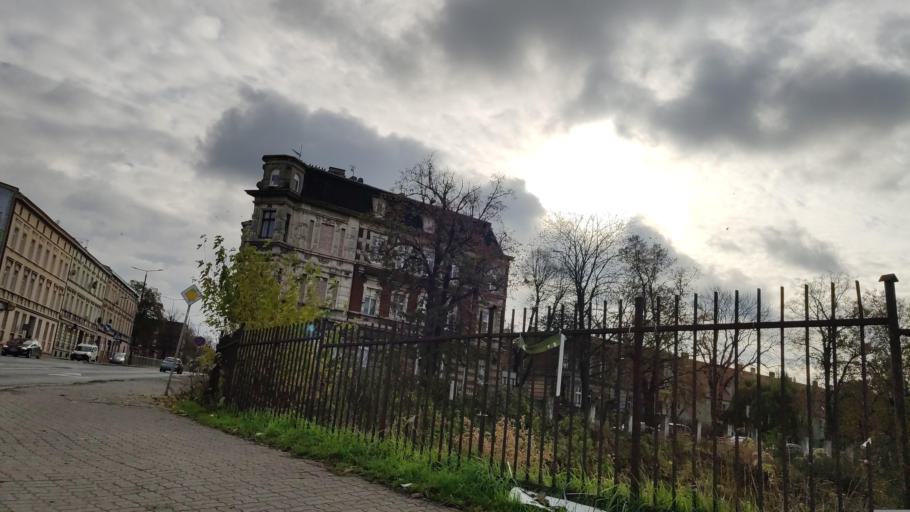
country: PL
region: Kujawsko-Pomorskie
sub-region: Powiat inowroclawski
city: Inowroclaw
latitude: 52.8057
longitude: 18.2471
